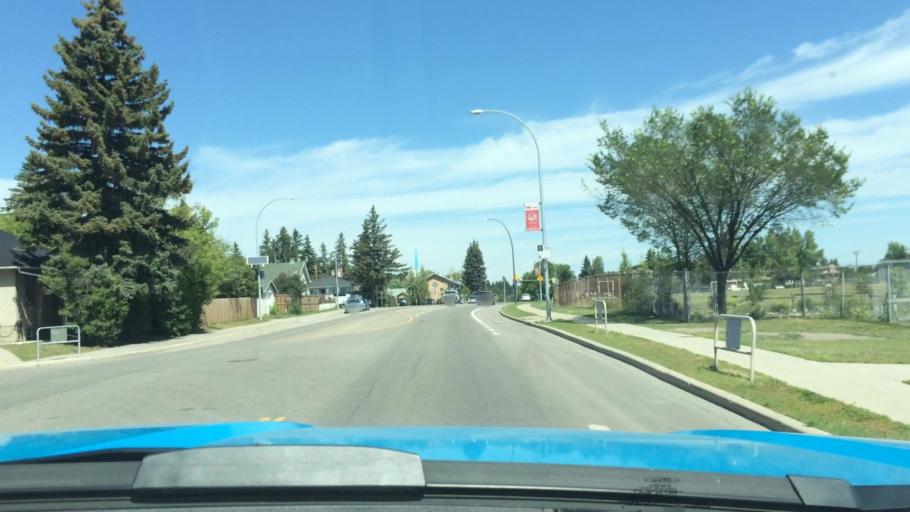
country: CA
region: Alberta
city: Calgary
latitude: 51.0713
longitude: -114.0848
